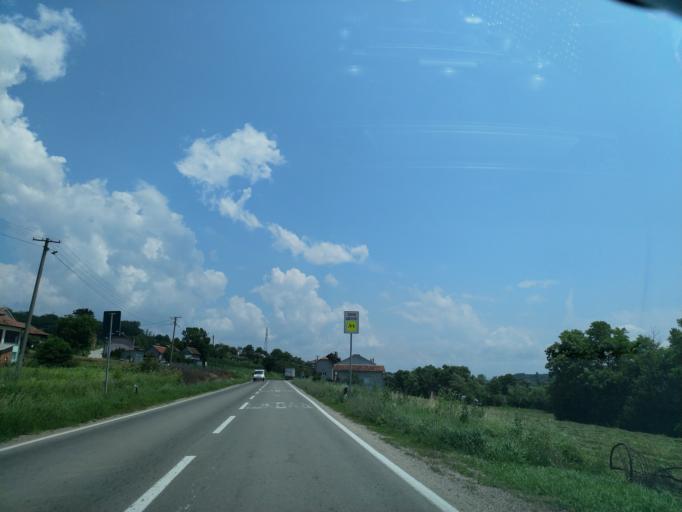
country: RS
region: Central Serbia
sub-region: Toplicki Okrug
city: Blace
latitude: 43.3056
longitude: 21.2523
